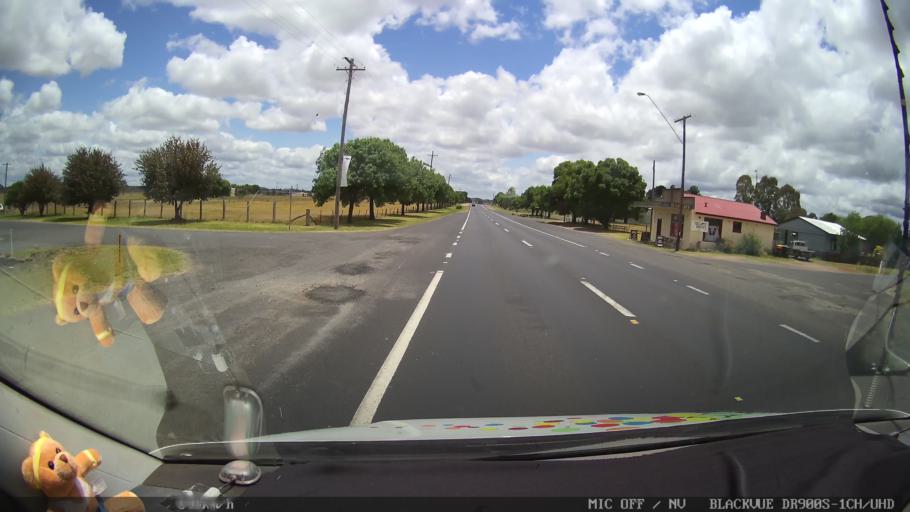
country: AU
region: New South Wales
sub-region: Glen Innes Severn
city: Glen Innes
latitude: -29.4395
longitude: 151.8466
